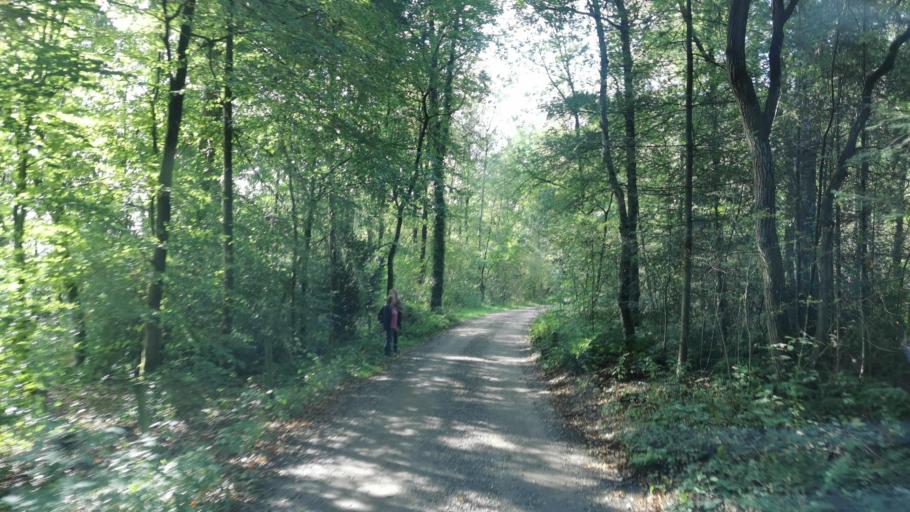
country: NL
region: Overijssel
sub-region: Gemeente Losser
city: Losser
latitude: 52.2764
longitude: 6.9645
